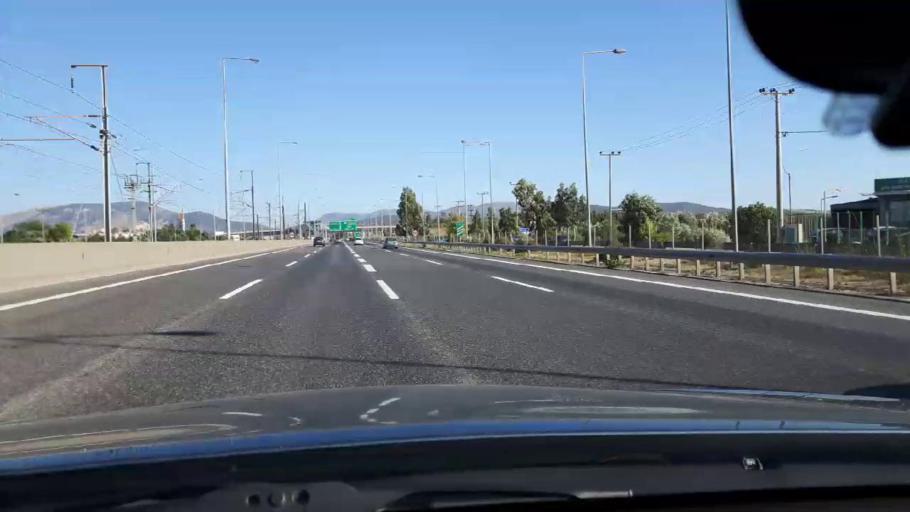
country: GR
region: Attica
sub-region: Nomarchia Anatolikis Attikis
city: Koropi
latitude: 37.9073
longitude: 23.9001
